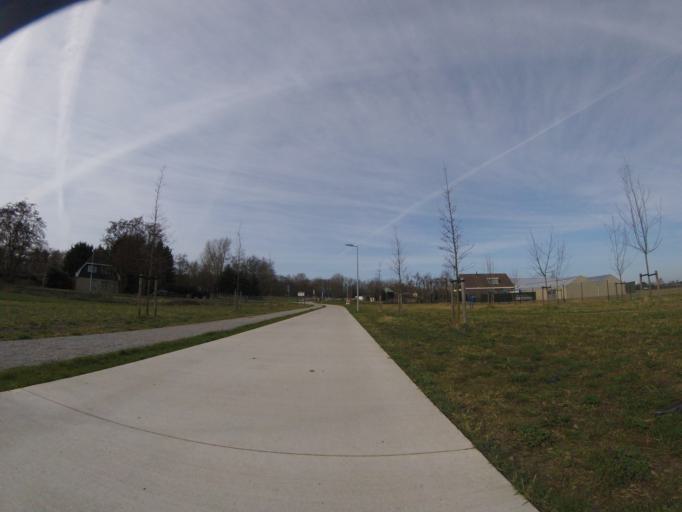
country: NL
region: North Holland
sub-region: Gemeente Bloemendaal
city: Bennebroek
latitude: 52.3193
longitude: 4.6142
